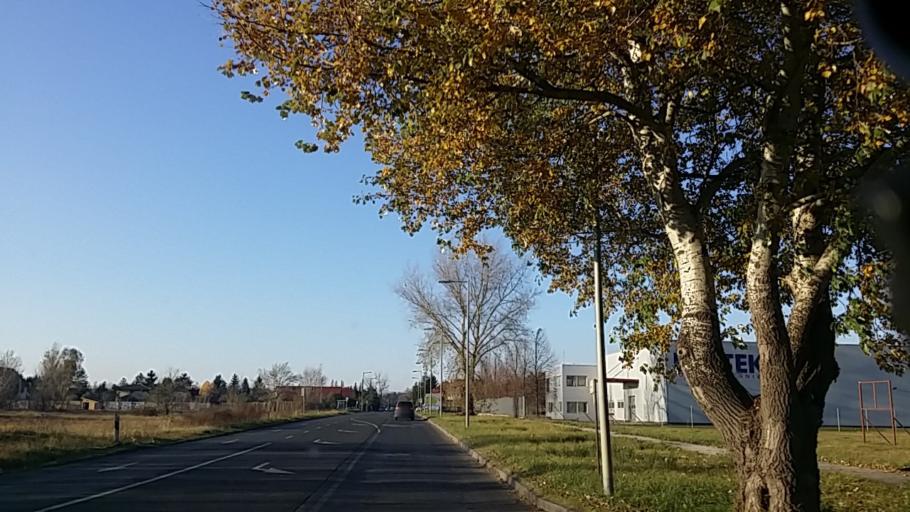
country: HU
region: Budapest
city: Budapest XVII. keruelet
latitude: 47.5015
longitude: 19.2159
